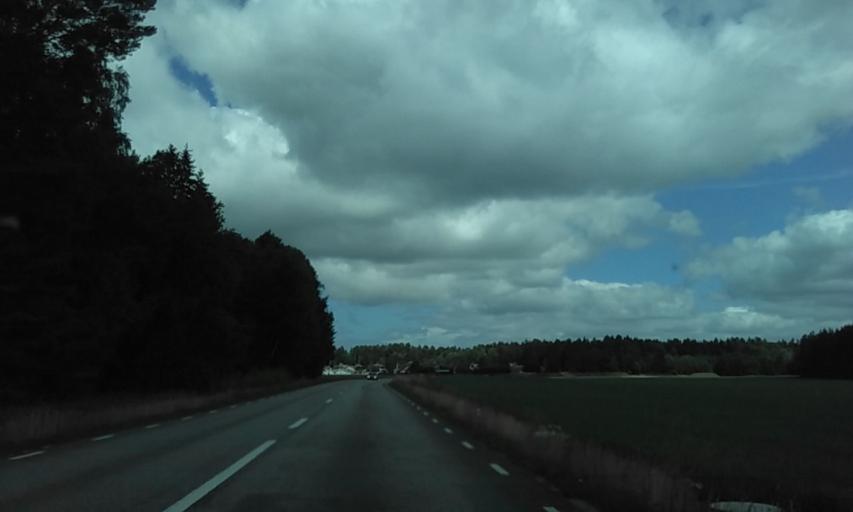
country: SE
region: Vaestra Goetaland
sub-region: Grastorps Kommun
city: Graestorp
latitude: 58.3186
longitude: 12.6751
